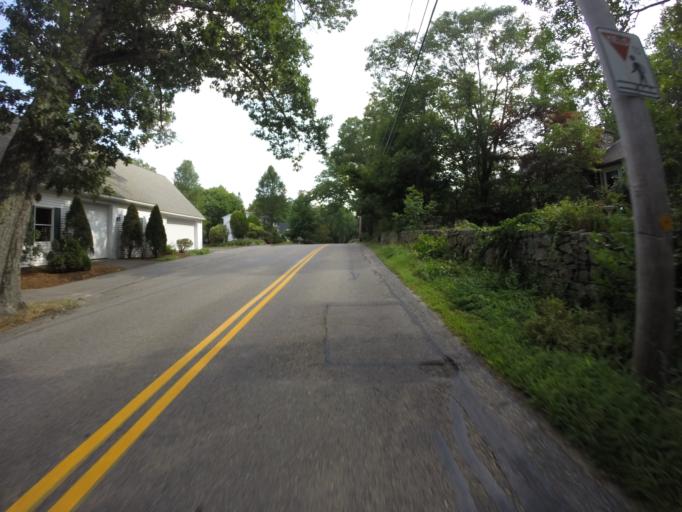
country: US
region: Massachusetts
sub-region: Norfolk County
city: Stoughton
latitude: 42.0748
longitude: -71.1070
